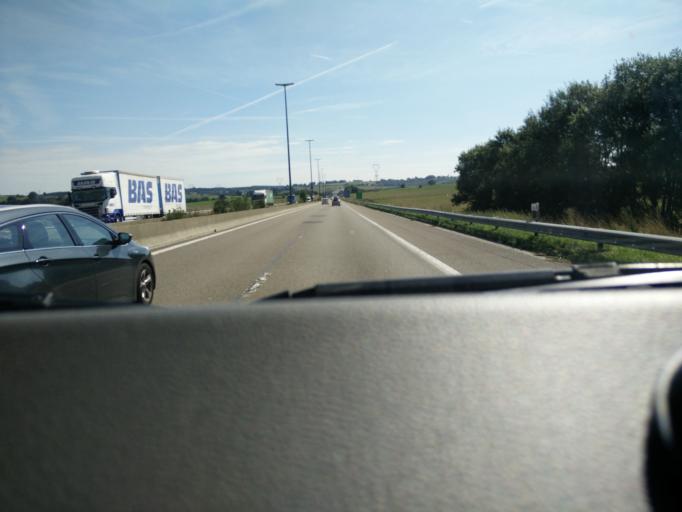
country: BE
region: Wallonia
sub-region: Province du Luxembourg
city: Neufchateau
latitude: 49.8788
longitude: 5.4551
